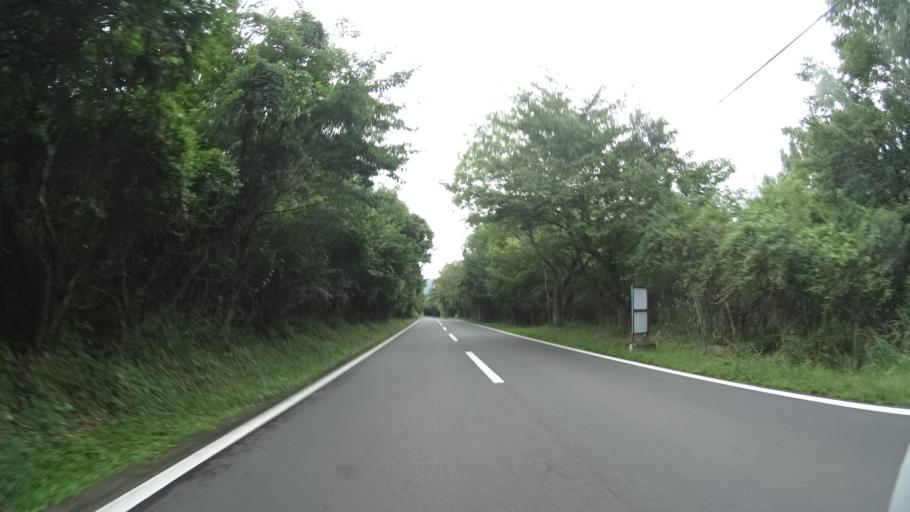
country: JP
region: Oita
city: Beppu
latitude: 33.3015
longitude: 131.3815
